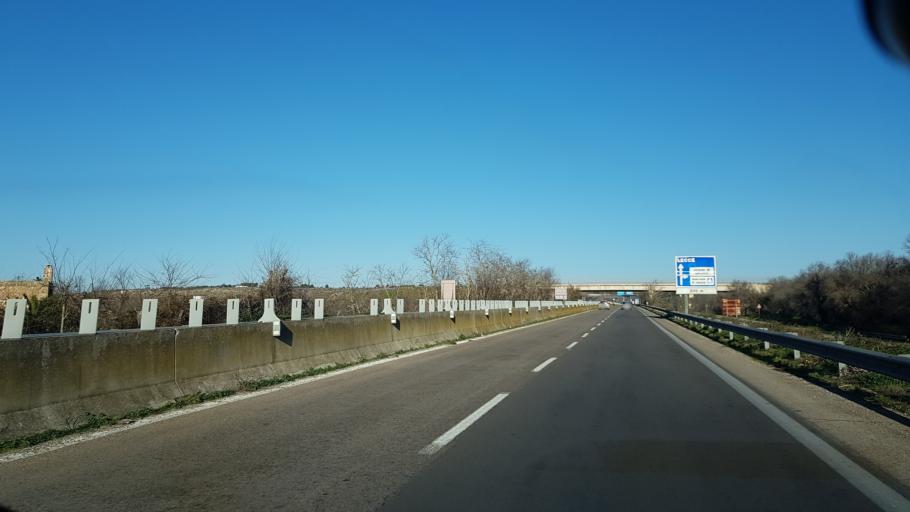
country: IT
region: Apulia
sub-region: Provincia di Lecce
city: Gallipoli
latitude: 40.0809
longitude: 18.0201
